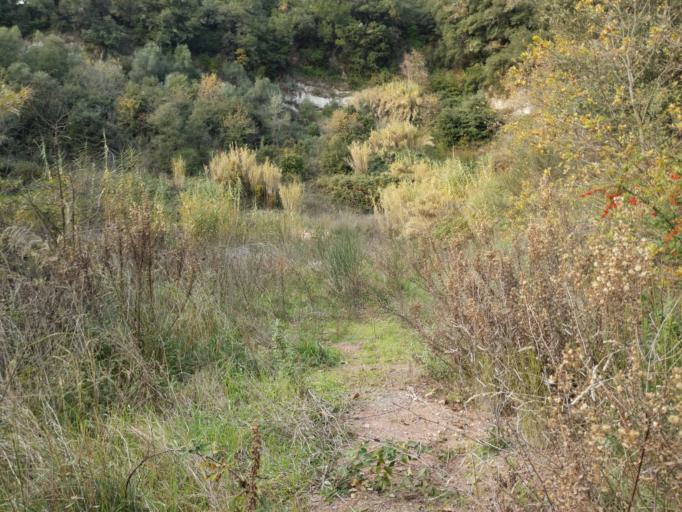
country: FR
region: Provence-Alpes-Cote d'Azur
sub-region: Departement du Var
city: Bagnols-en-Foret
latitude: 43.5409
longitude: 6.6953
